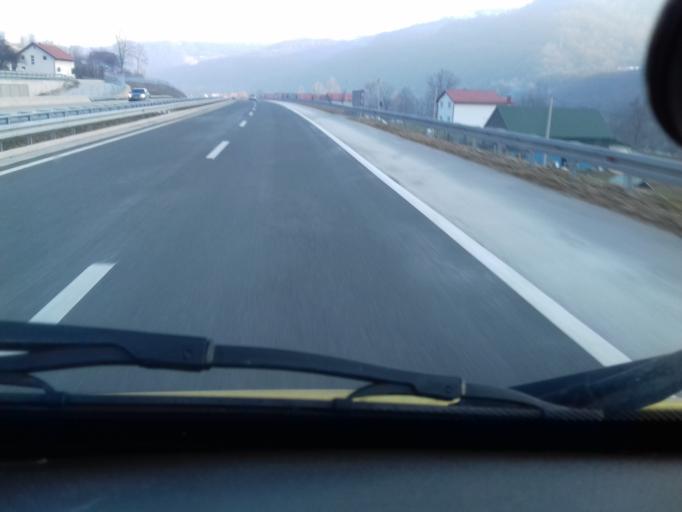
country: BA
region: Federation of Bosnia and Herzegovina
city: Kakanj
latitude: 44.1346
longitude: 18.0514
